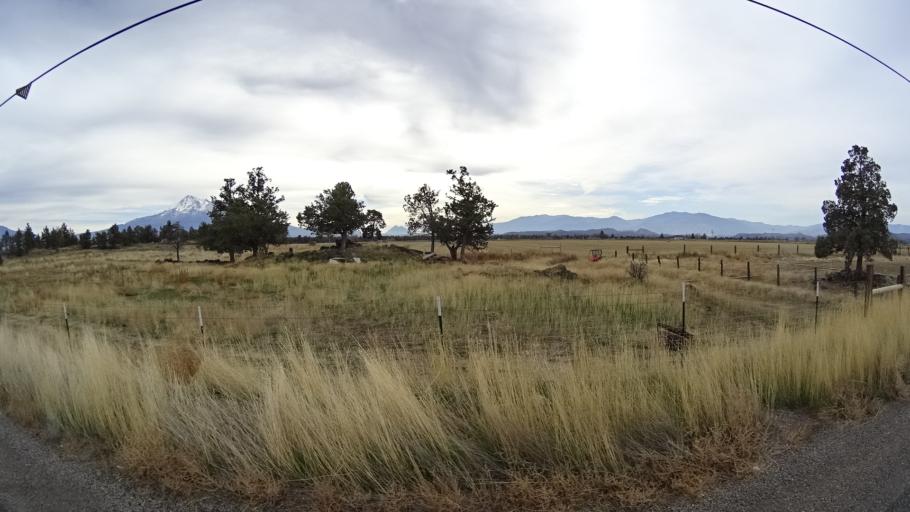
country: US
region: California
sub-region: Siskiyou County
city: Montague
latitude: 41.6238
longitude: -122.3869
